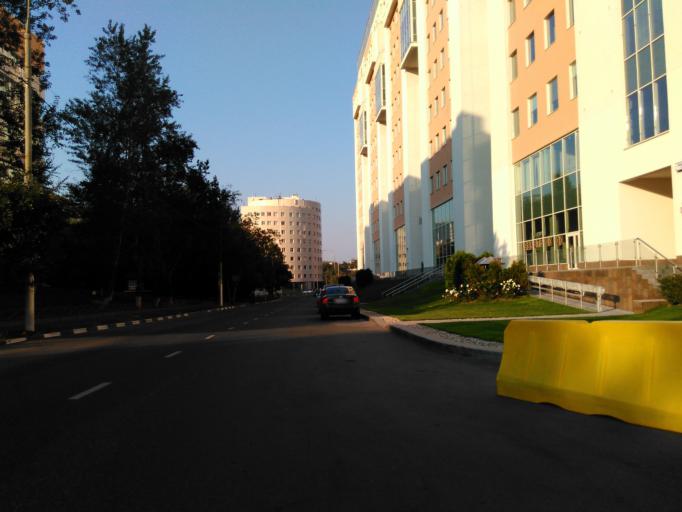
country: RU
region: Moskovskaya
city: Cheremushki
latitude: 55.6539
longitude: 37.5546
